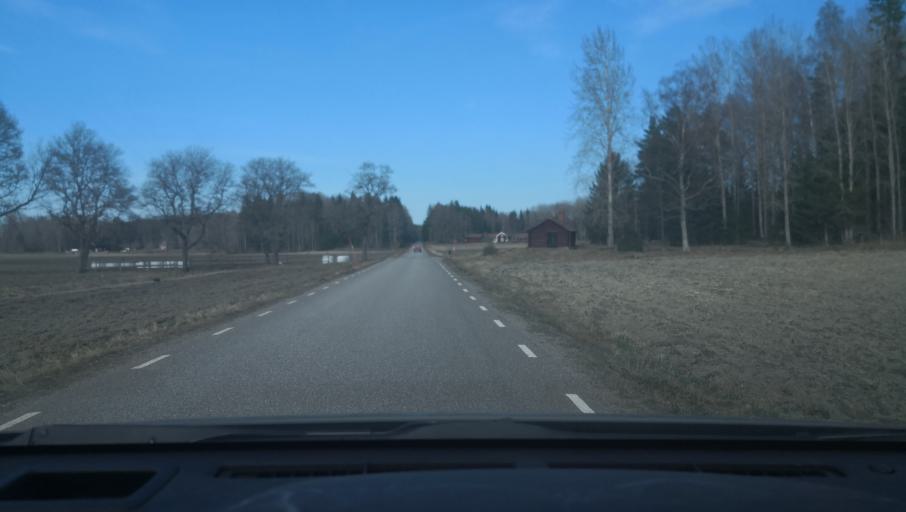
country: SE
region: Uppsala
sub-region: Heby Kommun
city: Heby
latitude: 59.9015
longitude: 16.8087
